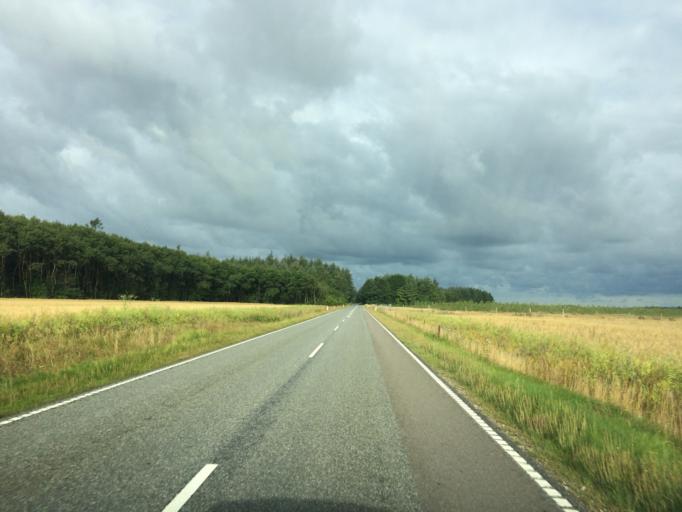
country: DK
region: Central Jutland
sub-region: Holstebro Kommune
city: Ulfborg
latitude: 56.1939
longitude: 8.3418
